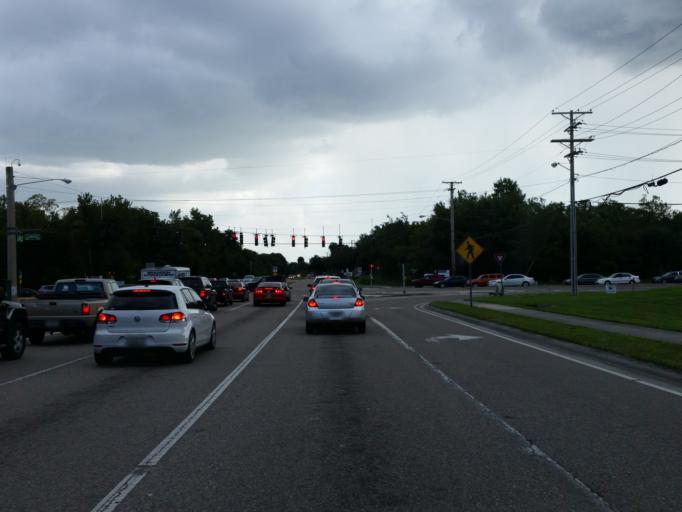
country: US
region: Florida
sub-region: Hillsborough County
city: Brandon
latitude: 27.9239
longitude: -82.2940
